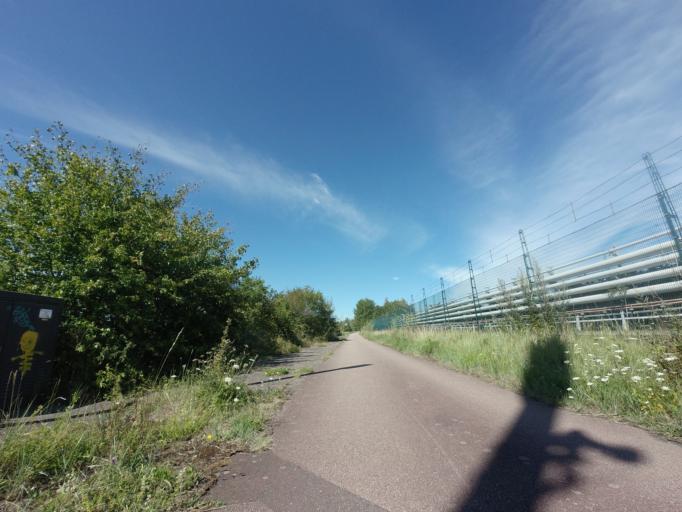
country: GB
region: England
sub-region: Kent
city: Sandwich
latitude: 51.2935
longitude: 1.3464
